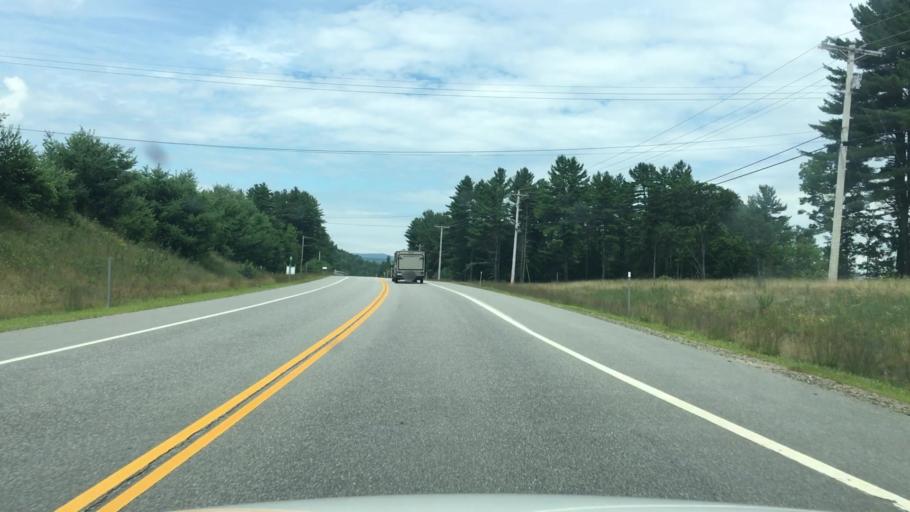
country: US
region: New Hampshire
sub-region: Grafton County
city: Rumney
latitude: 43.8277
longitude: -71.8942
